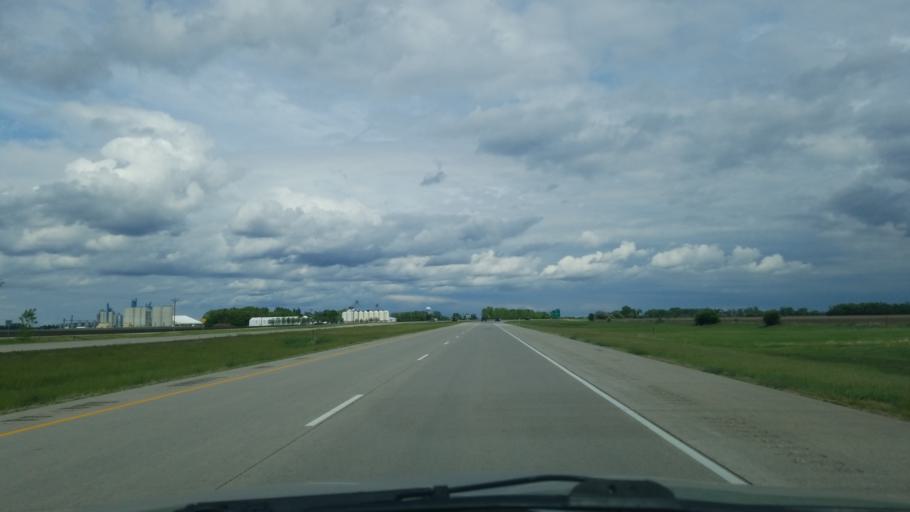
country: US
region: North Dakota
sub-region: Cass County
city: Casselton
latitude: 46.8759
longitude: -97.2435
